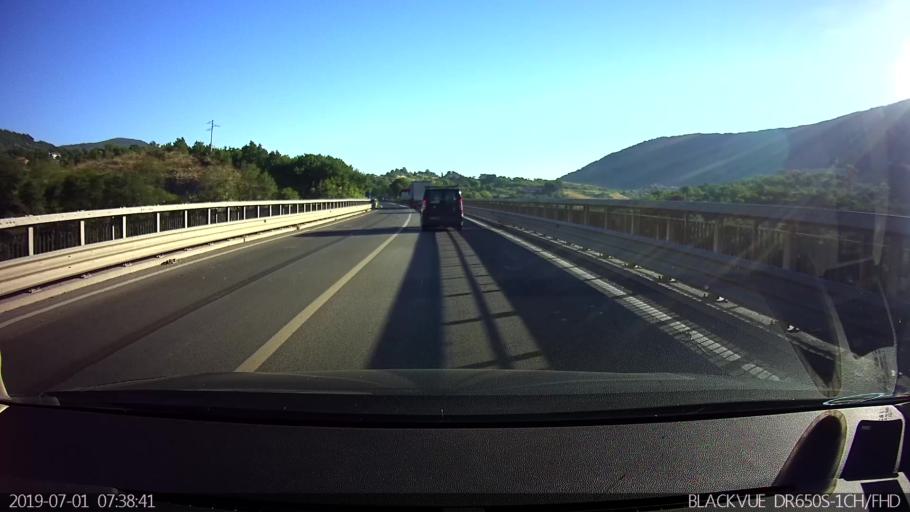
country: IT
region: Latium
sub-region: Provincia di Frosinone
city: Giuliano di Roma
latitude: 41.5448
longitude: 13.2693
